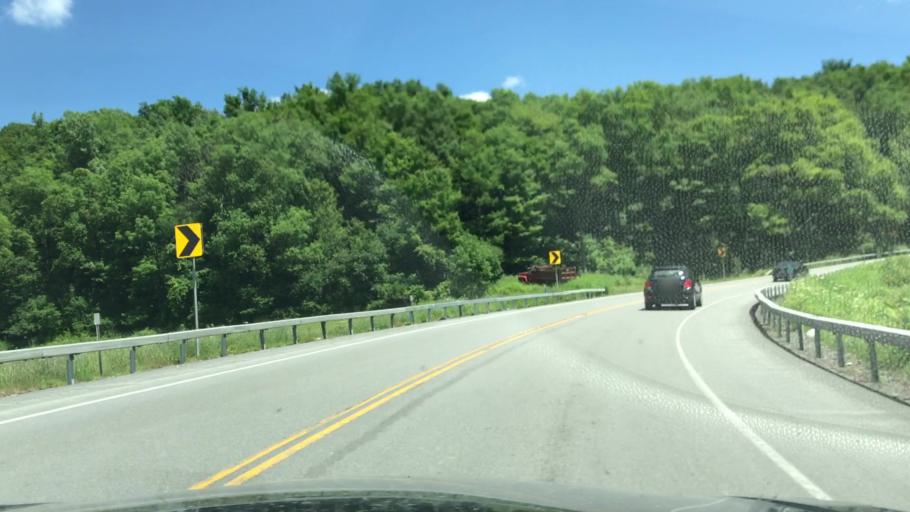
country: US
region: New York
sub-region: Wyoming County
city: Attica
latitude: 42.7733
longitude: -78.3722
